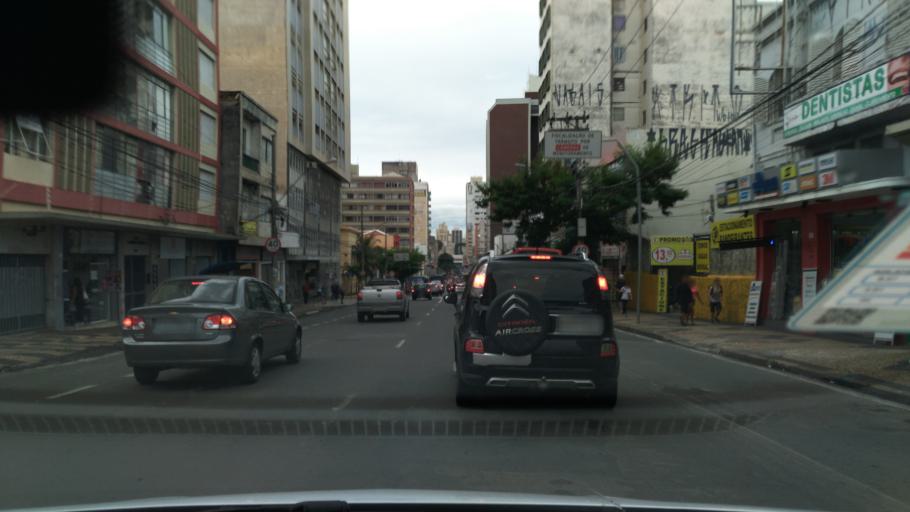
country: BR
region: Sao Paulo
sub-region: Campinas
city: Campinas
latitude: -22.9068
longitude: -47.0653
